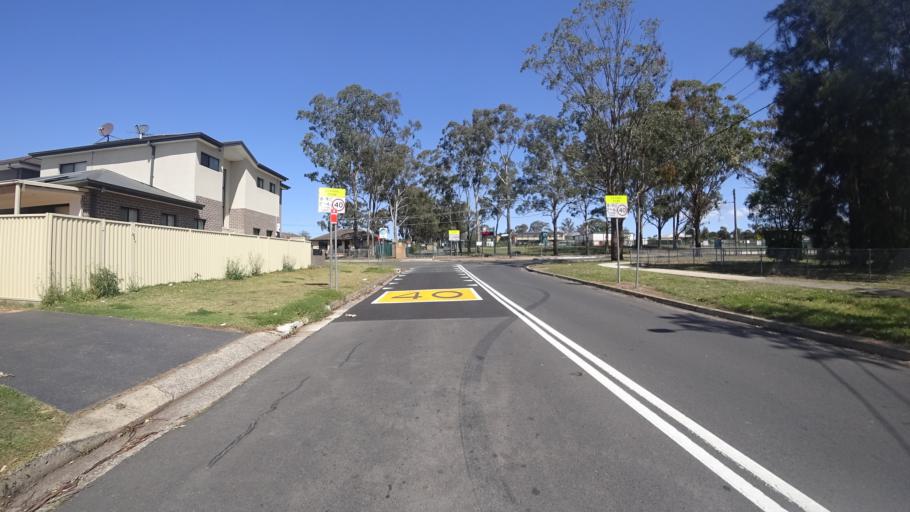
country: AU
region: New South Wales
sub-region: Liverpool
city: Miller
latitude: -33.9401
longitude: 150.8977
